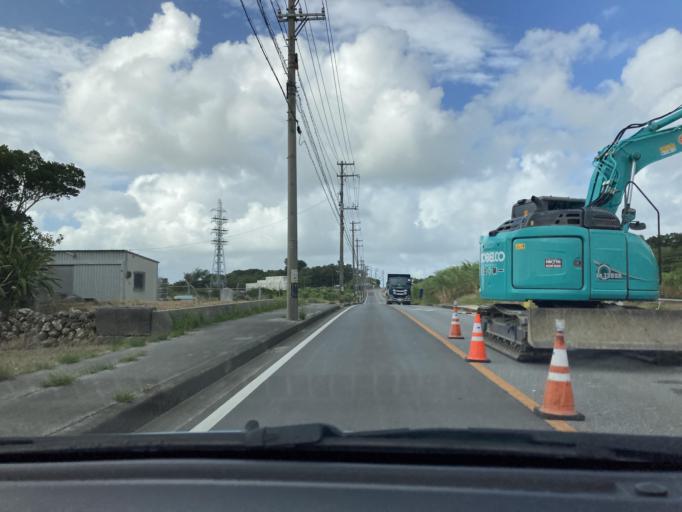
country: JP
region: Okinawa
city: Itoman
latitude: 26.1061
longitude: 127.6949
